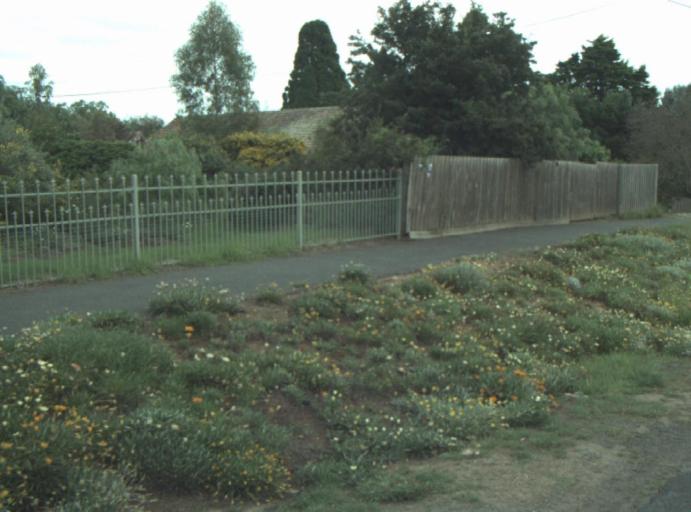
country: AU
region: Victoria
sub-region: Greater Geelong
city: Lara
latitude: -38.0333
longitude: 144.4123
